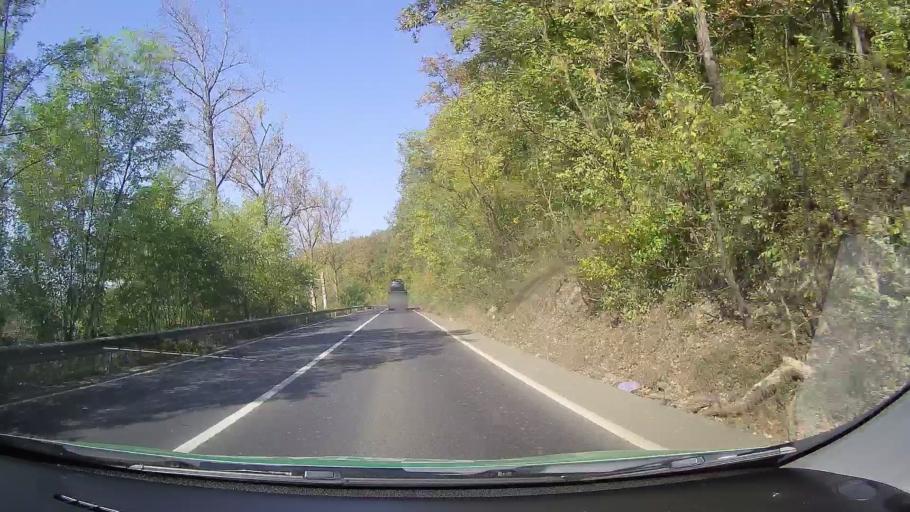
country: RO
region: Arad
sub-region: Comuna Varadia de Mures
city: Varadia de Mures
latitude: 46.0277
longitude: 22.1218
